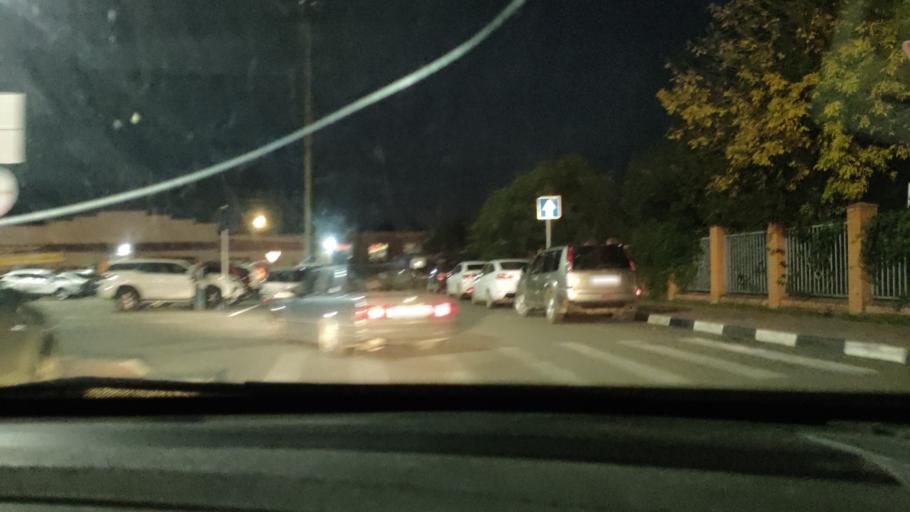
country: RU
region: Krasnodarskiy
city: Krasnodar
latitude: 45.1016
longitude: 38.9884
